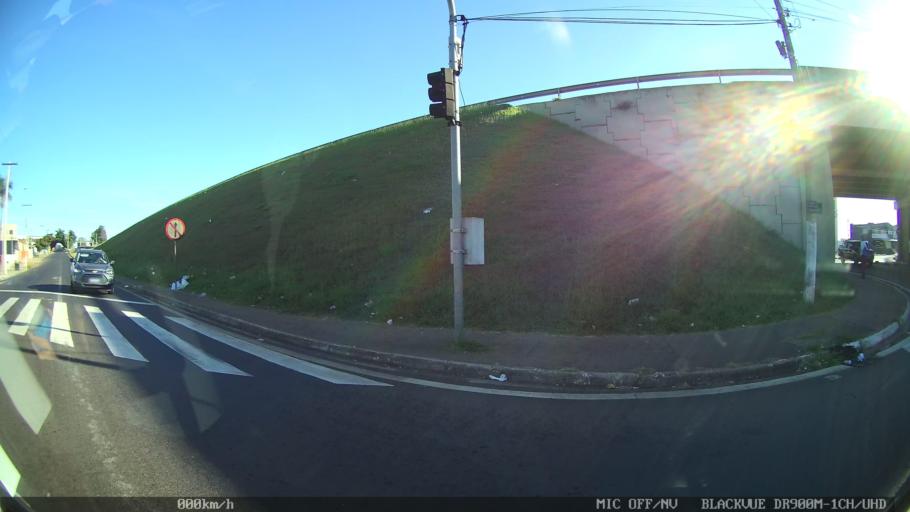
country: BR
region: Sao Paulo
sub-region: Franca
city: Franca
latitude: -20.5738
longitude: -47.3725
